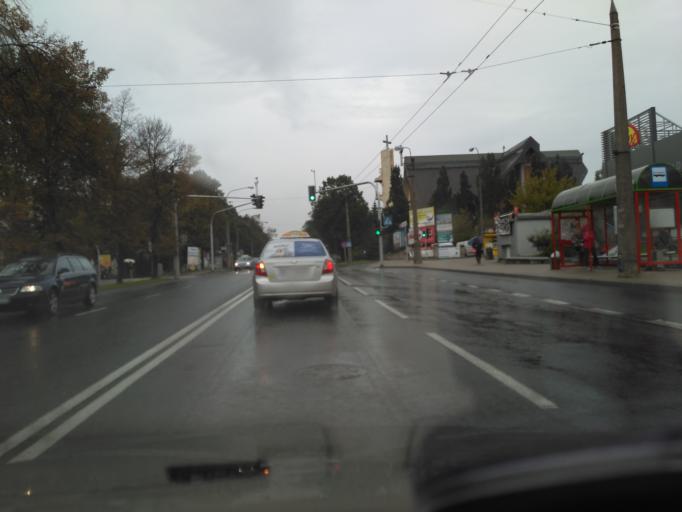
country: PL
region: Lublin Voivodeship
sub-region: Powiat lubelski
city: Lublin
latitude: 51.2334
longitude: 22.5855
